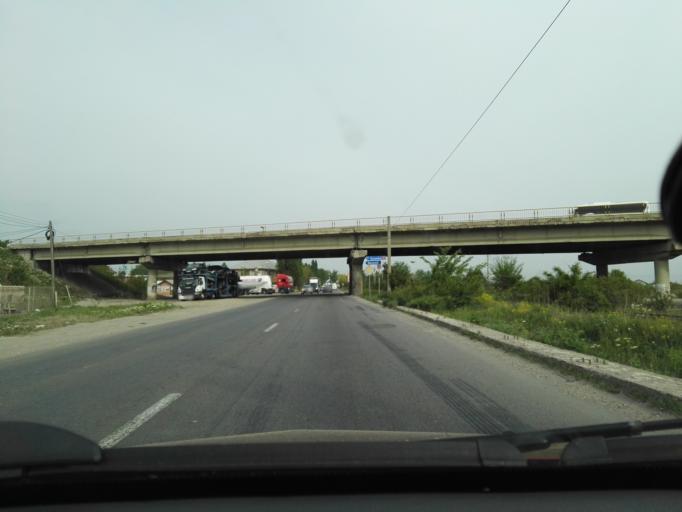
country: RO
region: Ilfov
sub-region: Comuna Bragadiru
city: Bragadiru
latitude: 44.3826
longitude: 25.9944
